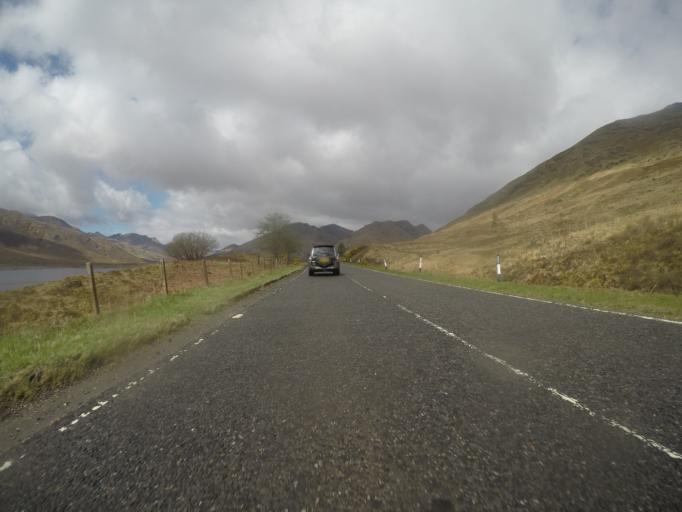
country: GB
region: Scotland
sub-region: Highland
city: Fort William
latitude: 57.1548
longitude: -5.1384
